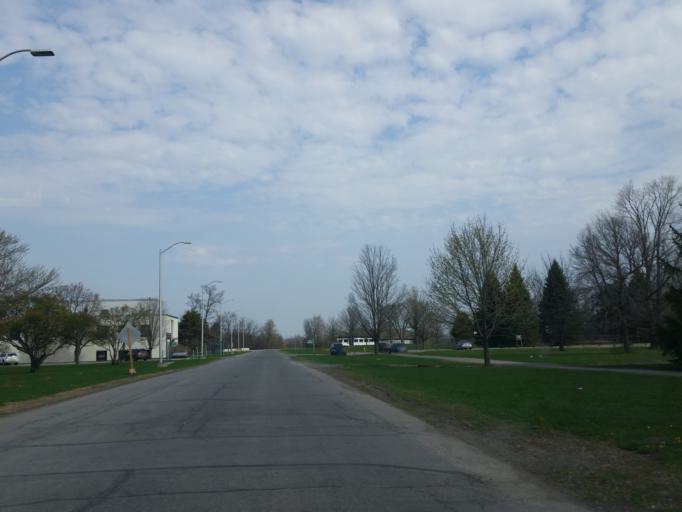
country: CA
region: Quebec
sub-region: Outaouais
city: Gatineau
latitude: 45.4534
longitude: -75.6221
